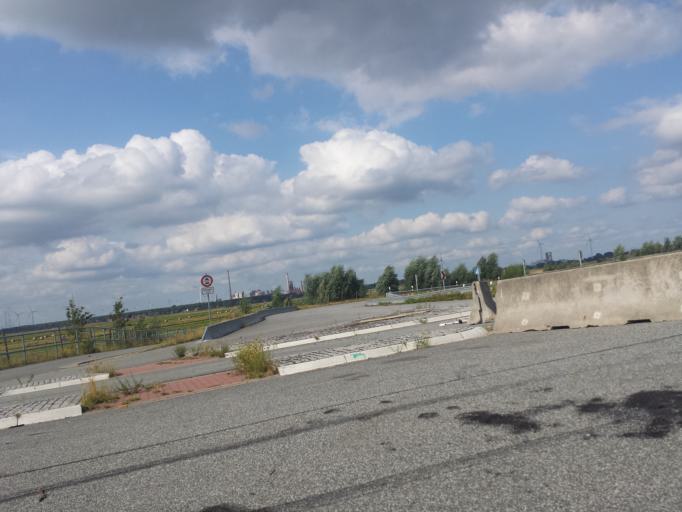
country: DE
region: Lower Saxony
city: Delmenhorst
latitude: 53.0966
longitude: 8.6874
